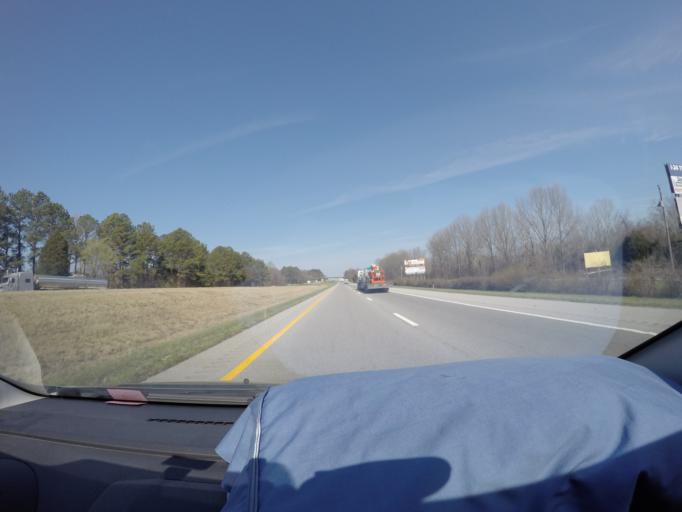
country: US
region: Tennessee
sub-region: Franklin County
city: Sewanee
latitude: 35.3597
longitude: -85.9579
